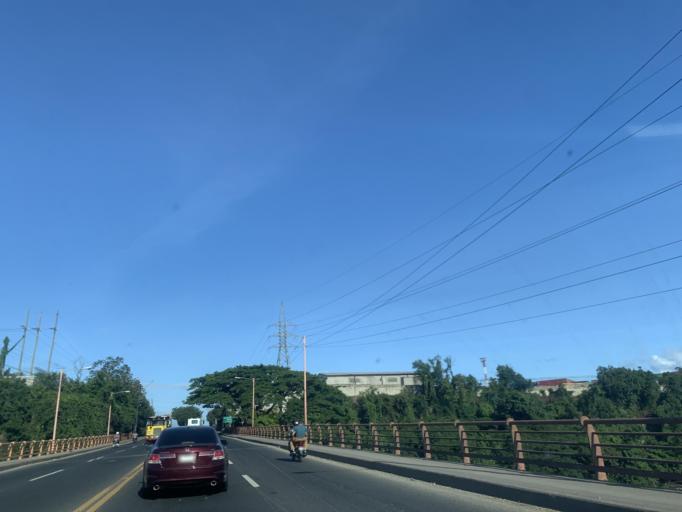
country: DO
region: San Cristobal
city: El Carril
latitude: 18.4315
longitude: -70.0063
